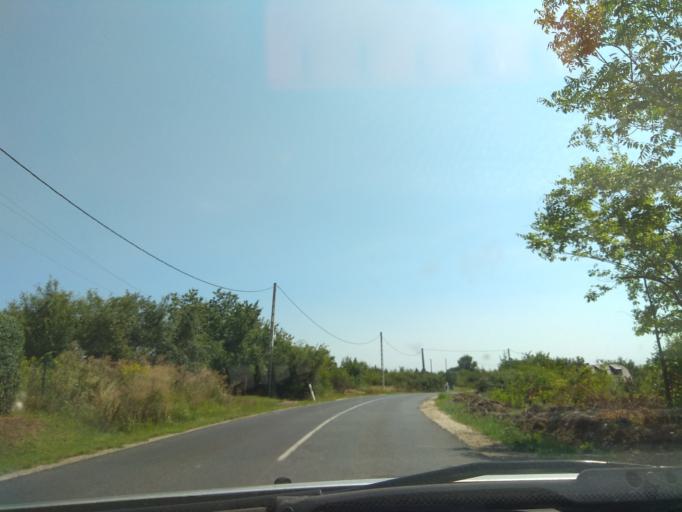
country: HU
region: Borsod-Abauj-Zemplen
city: Malyi
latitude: 48.0379
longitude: 20.7771
